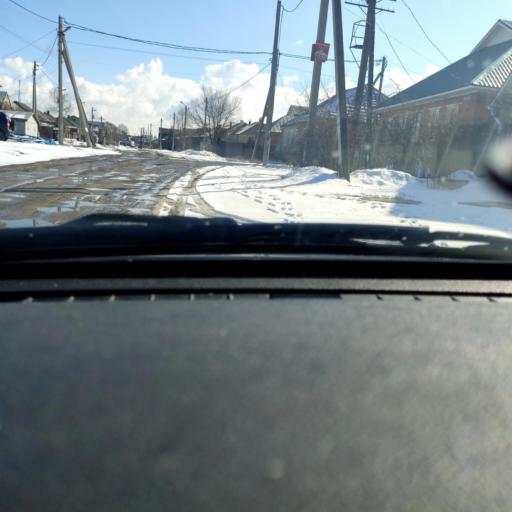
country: RU
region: Voronezj
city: Somovo
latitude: 51.7529
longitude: 39.3321
